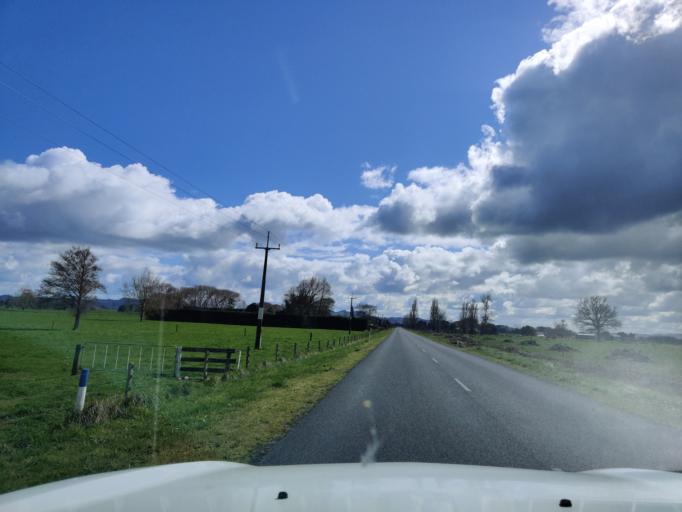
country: NZ
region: Waikato
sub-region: Waikato District
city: Ngaruawahia
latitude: -37.6012
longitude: 175.3007
